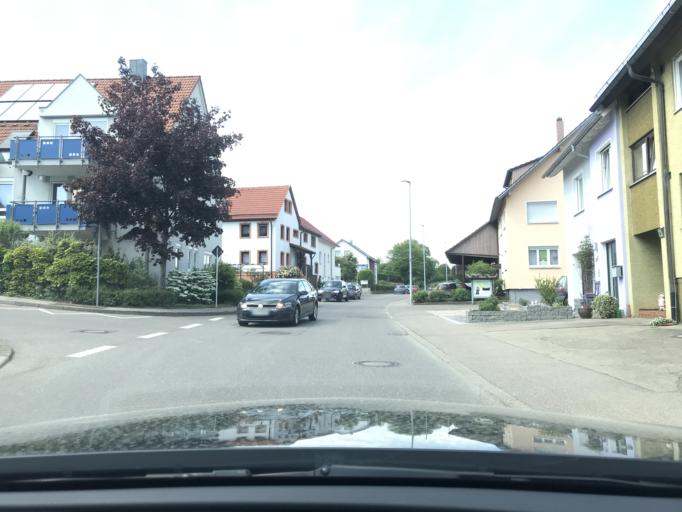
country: DE
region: Baden-Wuerttemberg
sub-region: Regierungsbezirk Stuttgart
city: Altbach
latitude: 48.7602
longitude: 9.3730
